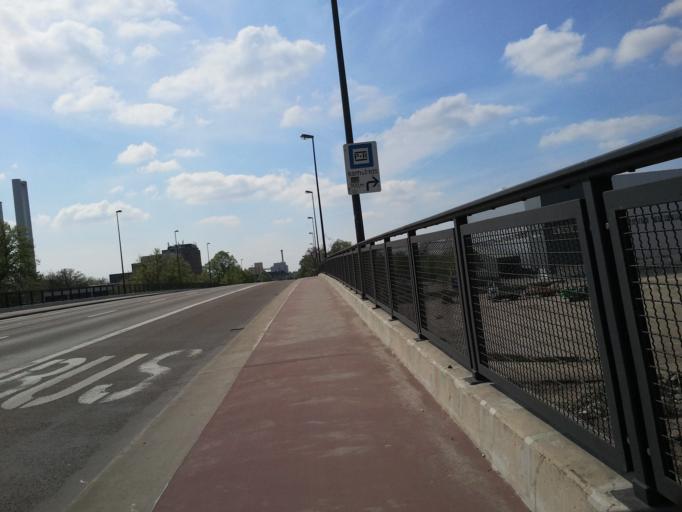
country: DE
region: Lower Saxony
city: Lilienthal
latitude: 53.0596
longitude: 8.9064
